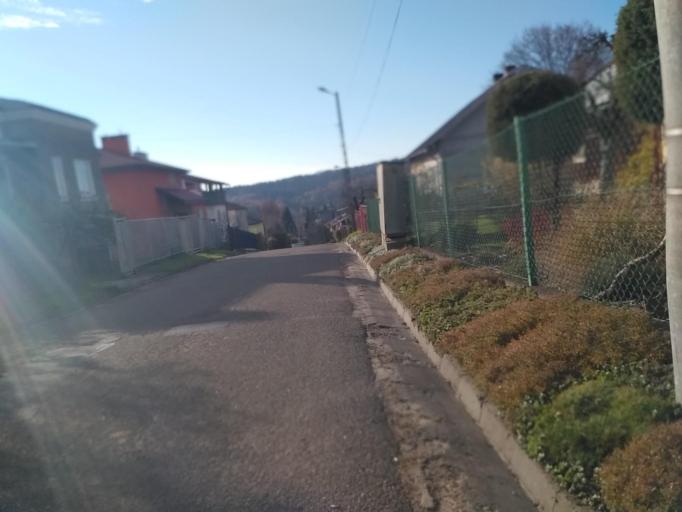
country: PL
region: Subcarpathian Voivodeship
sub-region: Powiat brzozowski
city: Brzozow
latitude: 49.6922
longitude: 22.0103
